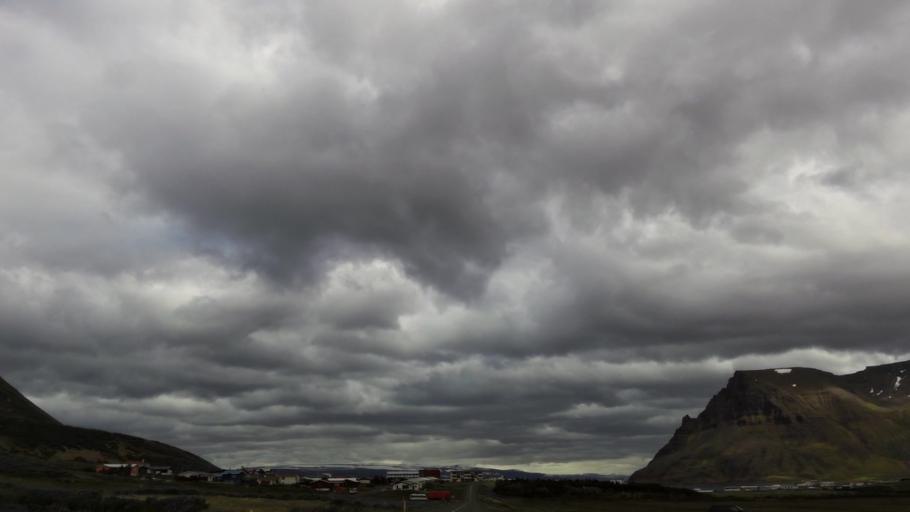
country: IS
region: Westfjords
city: Isafjoerdur
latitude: 66.1587
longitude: -23.2731
